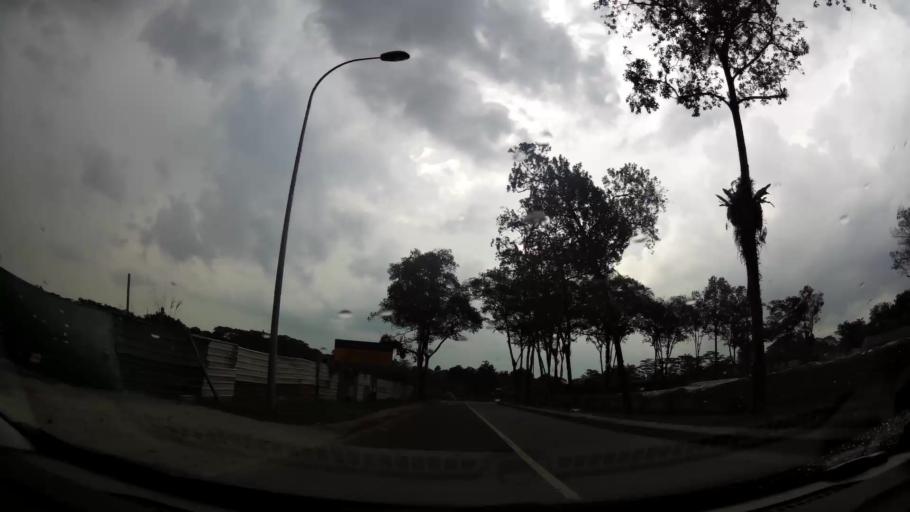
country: MY
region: Johor
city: Kampung Pasir Gudang Baru
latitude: 1.3941
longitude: 103.8703
